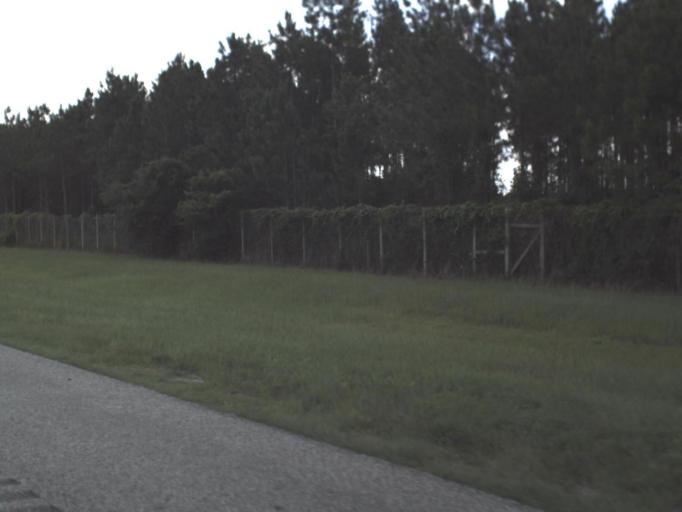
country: US
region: Florida
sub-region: Flagler County
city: Palm Coast
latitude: 29.6675
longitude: -81.2969
